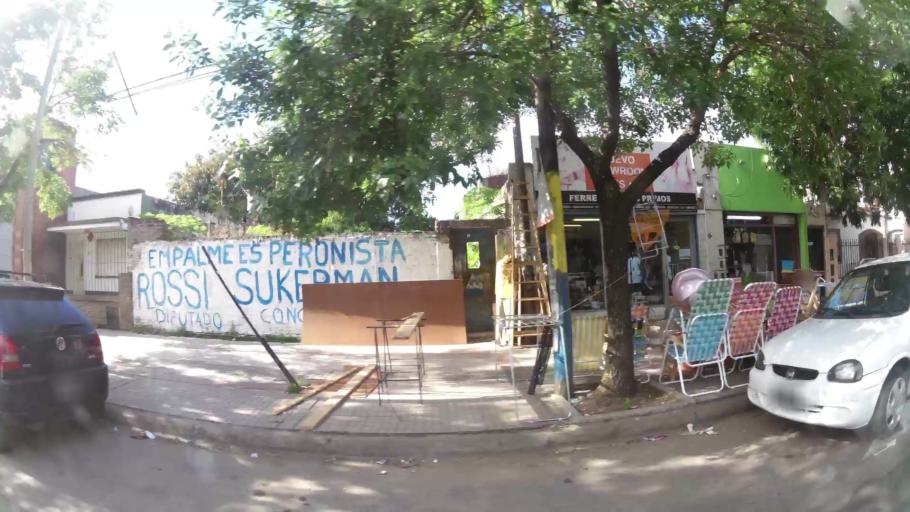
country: AR
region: Santa Fe
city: Granadero Baigorria
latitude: -32.9199
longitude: -60.7016
